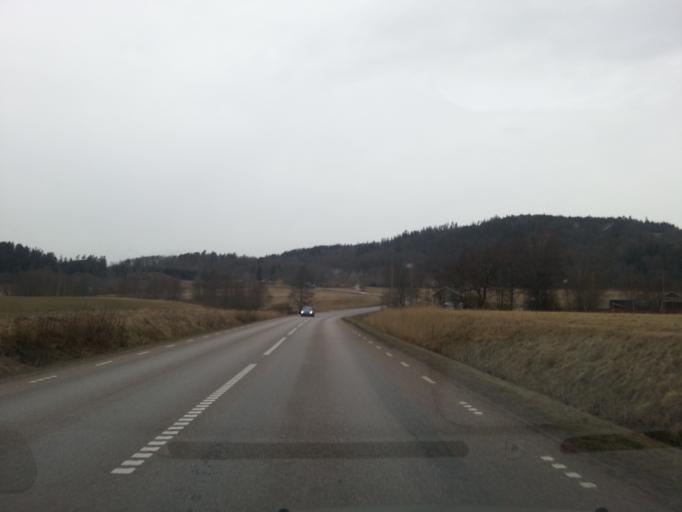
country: SE
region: Vaestra Goetaland
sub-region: Lilla Edets Kommun
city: Lilla Edet
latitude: 58.1416
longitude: 12.0963
